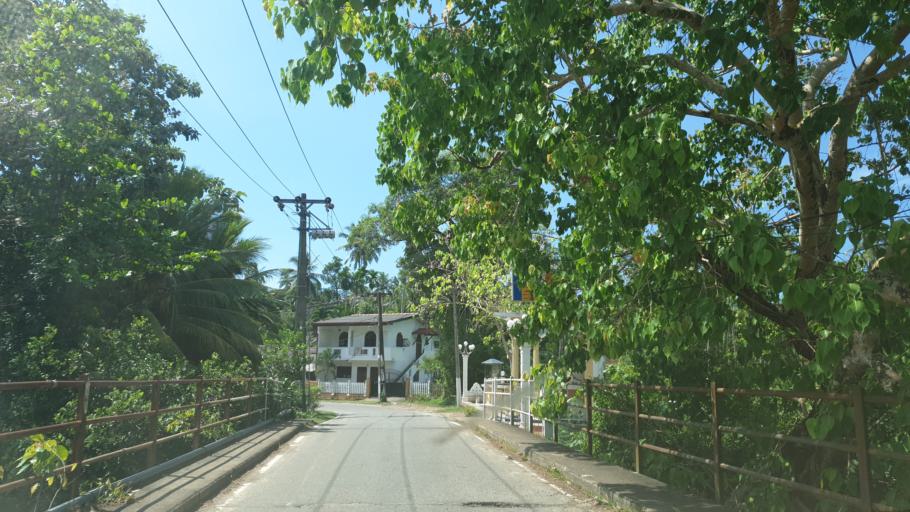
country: LK
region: Western
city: Panadura
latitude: 6.6831
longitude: 79.9297
